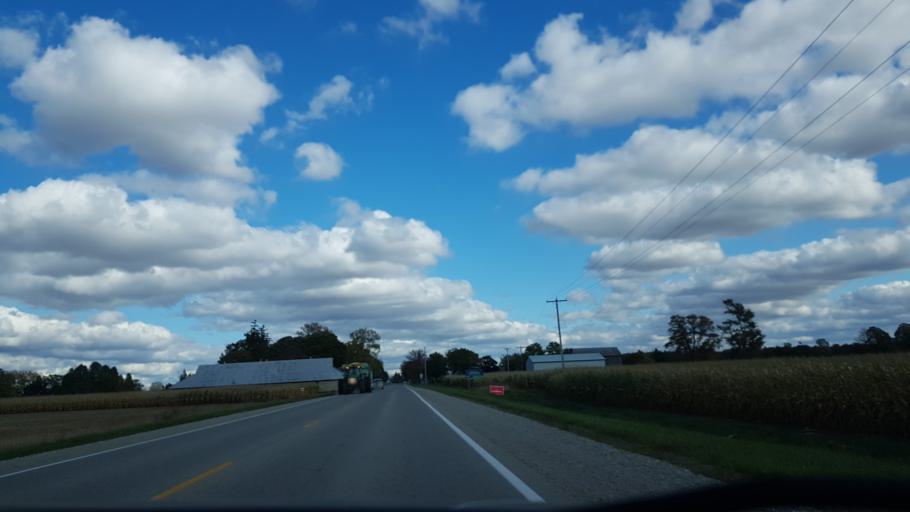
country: CA
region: Ontario
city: South Huron
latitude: 43.2424
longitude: -81.7207
